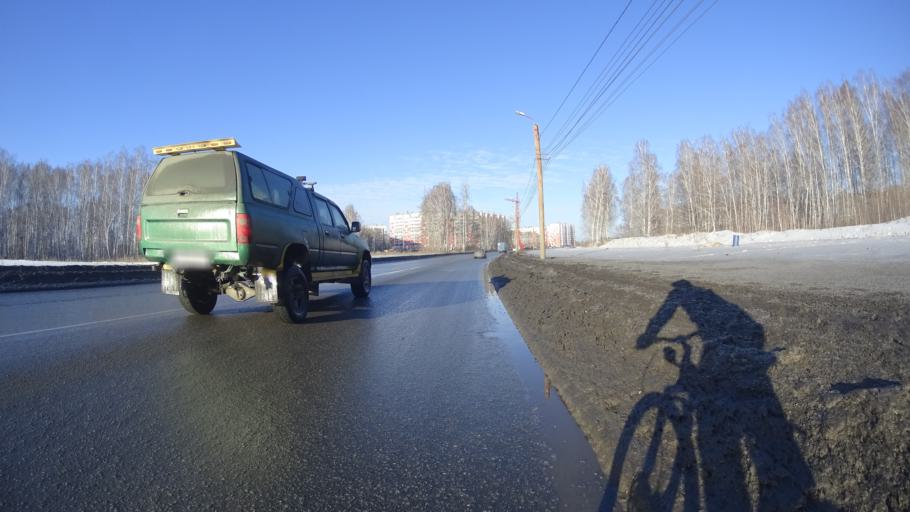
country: RU
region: Chelyabinsk
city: Roshchino
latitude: 55.2141
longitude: 61.2849
